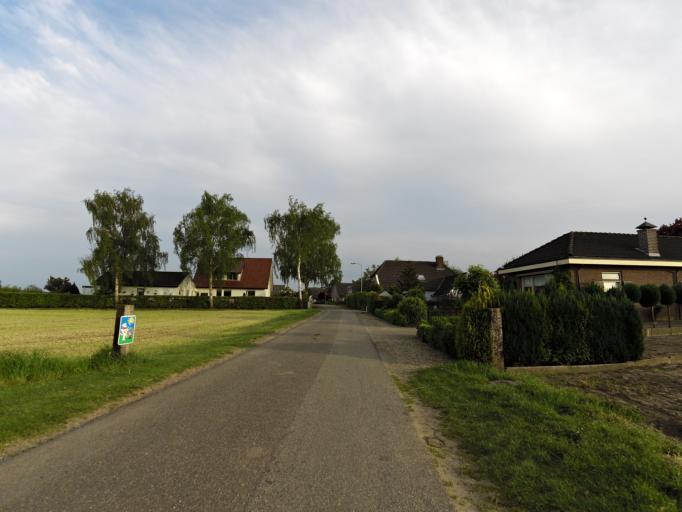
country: NL
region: Gelderland
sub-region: Oude IJsselstreek
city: Gendringen
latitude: 51.8693
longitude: 6.3624
